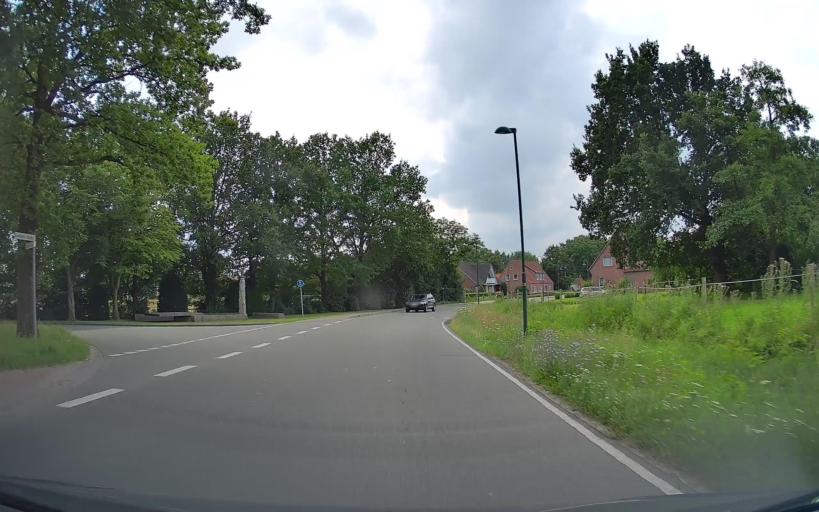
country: DE
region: Lower Saxony
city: Bosel
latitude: 53.0092
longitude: 7.9547
